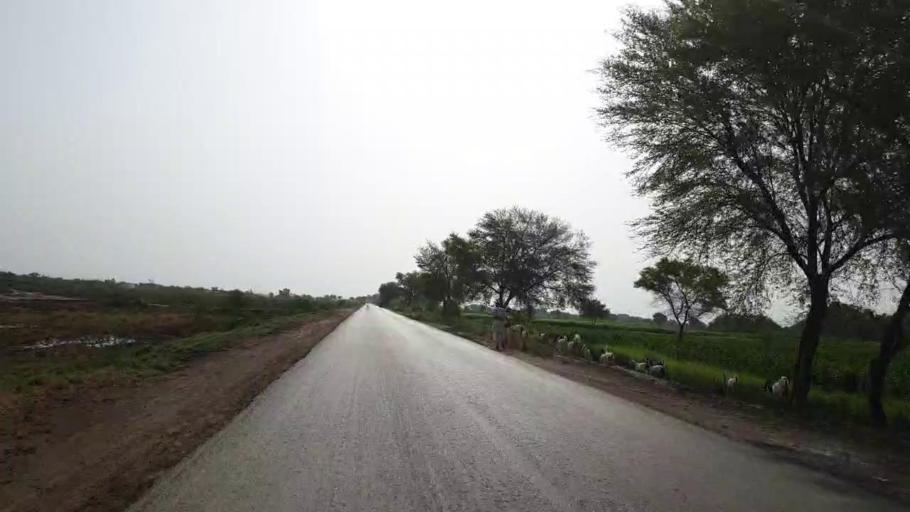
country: PK
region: Sindh
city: Nawabshah
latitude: 26.2585
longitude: 68.4775
